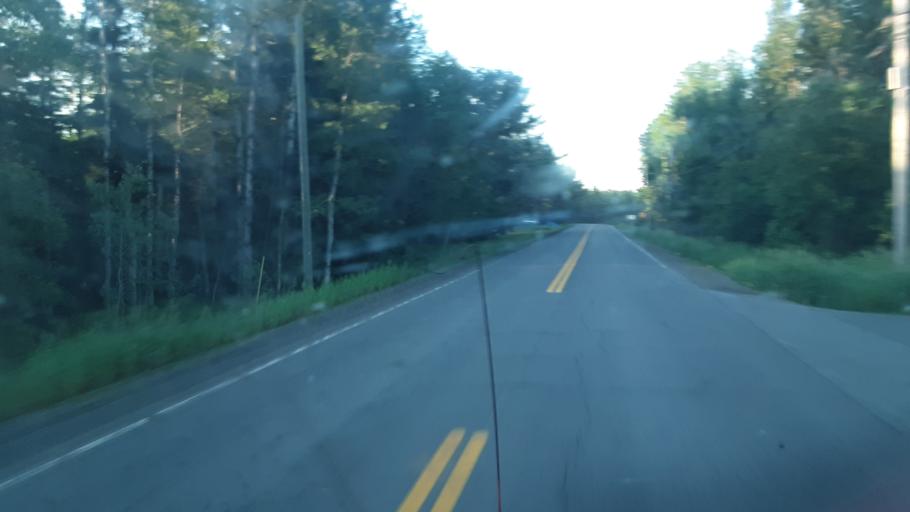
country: US
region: Maine
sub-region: Aroostook County
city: Presque Isle
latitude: 46.7329
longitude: -68.0302
